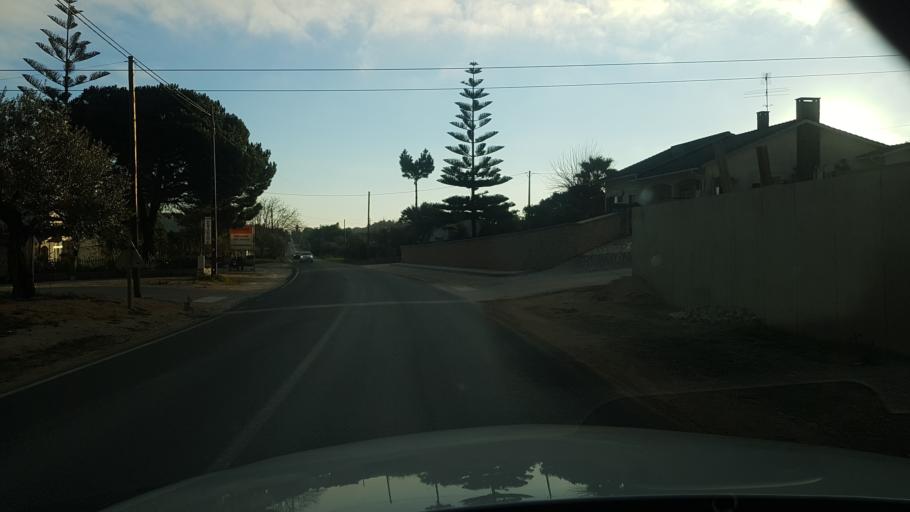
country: PT
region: Santarem
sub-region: Ourem
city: Ourem
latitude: 39.5719
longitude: -8.5998
